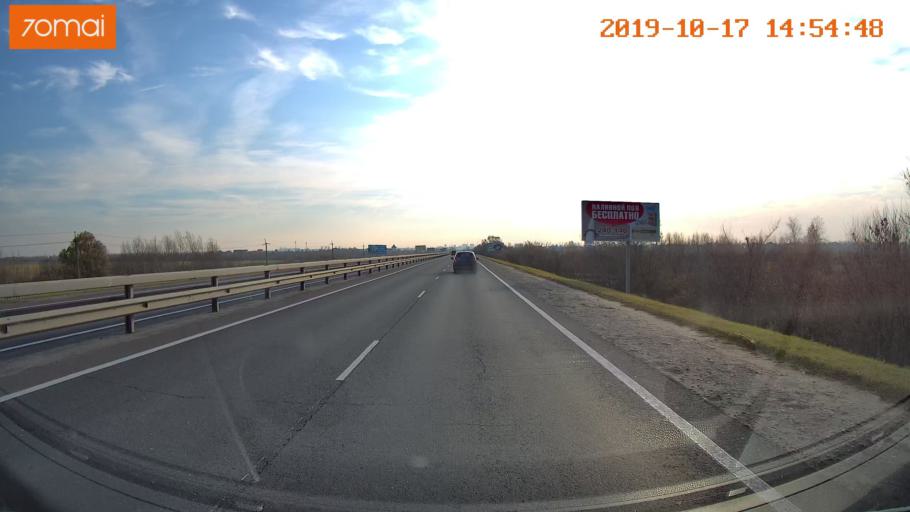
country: RU
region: Rjazan
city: Polyany
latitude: 54.6767
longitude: 39.8293
